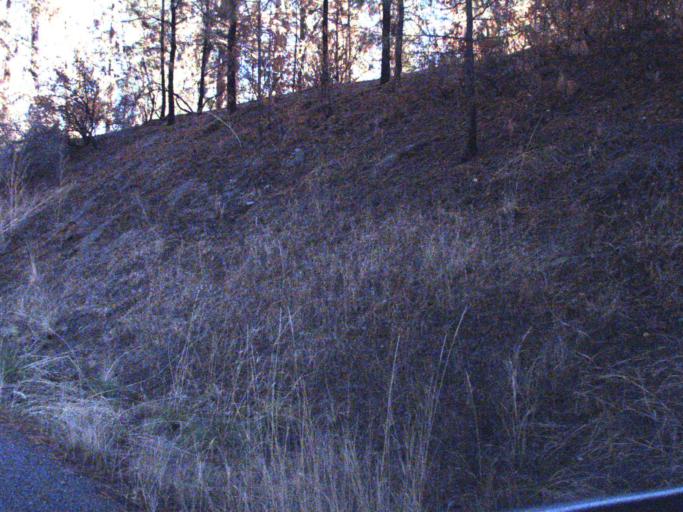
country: US
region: Washington
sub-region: Okanogan County
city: Coulee Dam
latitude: 48.0438
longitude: -118.6708
